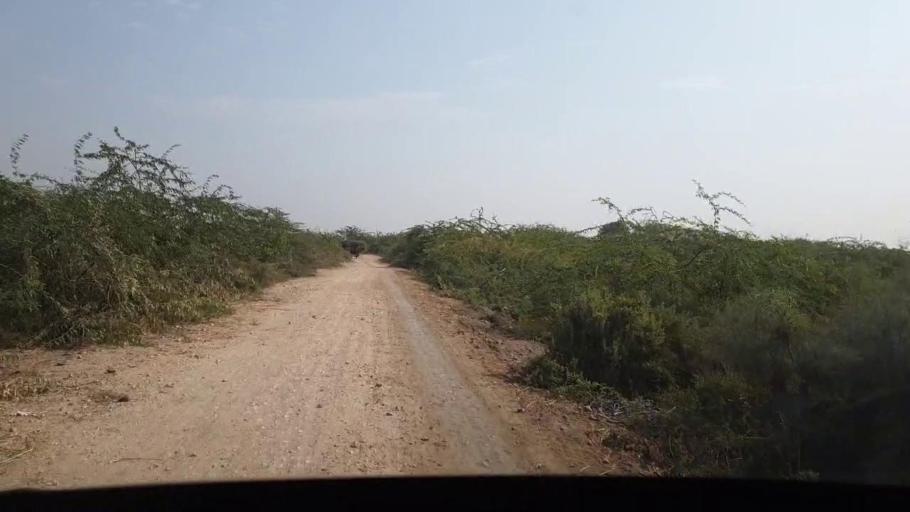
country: PK
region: Sindh
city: Chuhar Jamali
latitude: 24.2680
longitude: 67.9119
